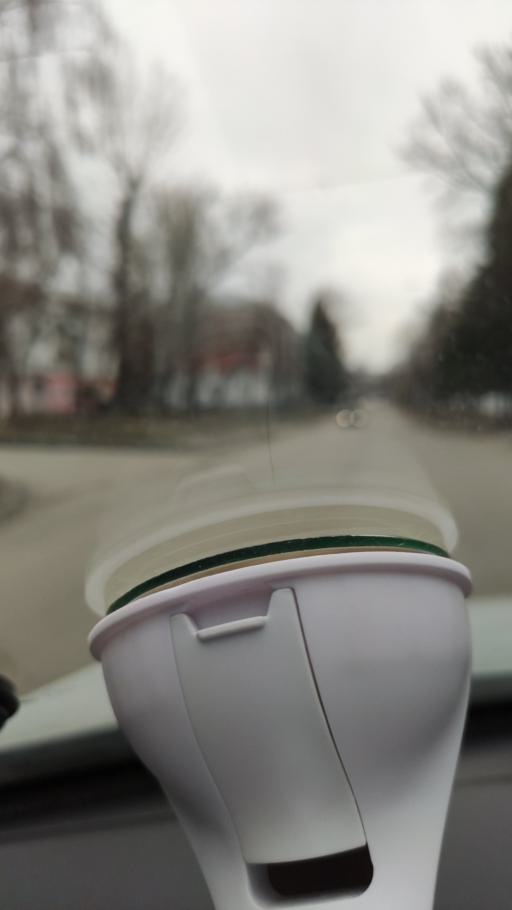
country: RU
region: Samara
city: Volzhskiy
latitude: 53.3450
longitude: 50.2162
